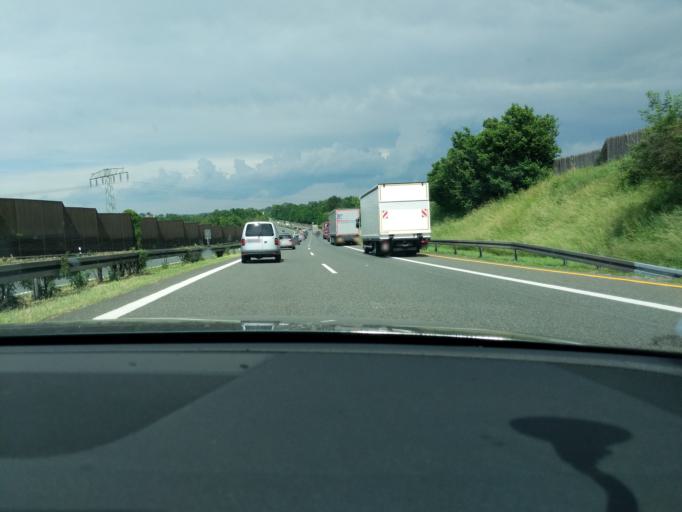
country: DE
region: Saxony
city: Wilkau-Hasslau
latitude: 50.6638
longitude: 12.5146
